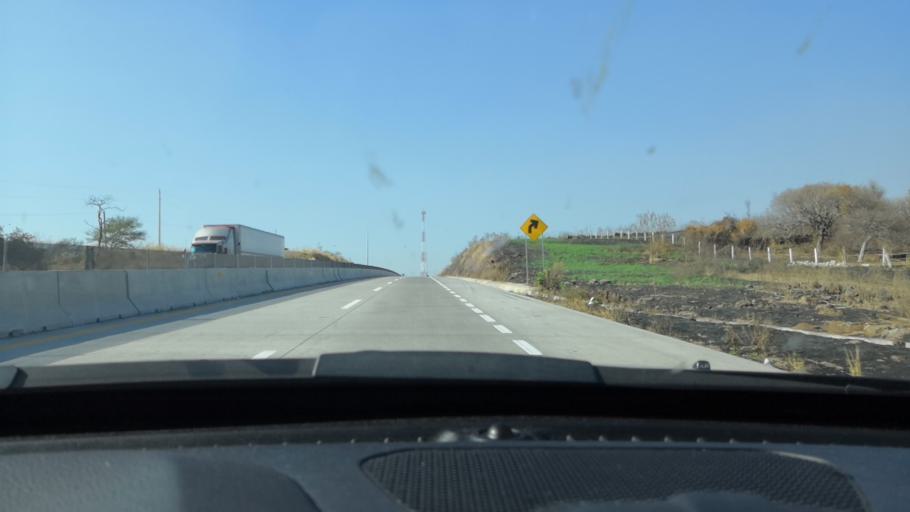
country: MX
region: Jalisco
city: Zapotlanejo
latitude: 20.6009
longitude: -103.1017
